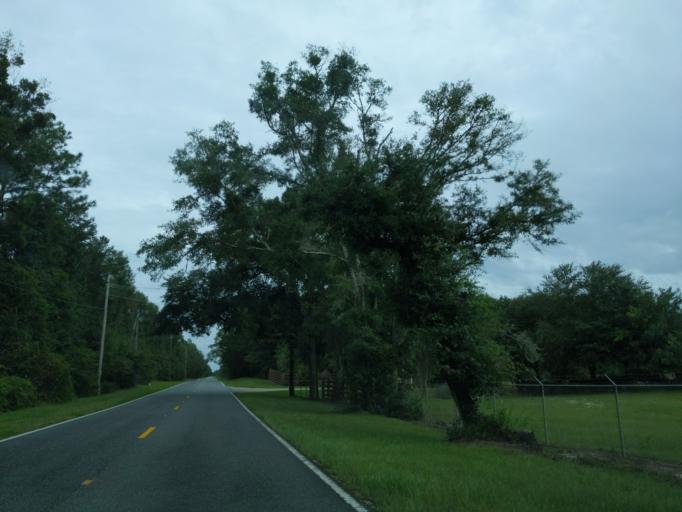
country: US
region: Florida
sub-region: Leon County
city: Woodville
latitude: 30.3719
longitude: -84.1958
